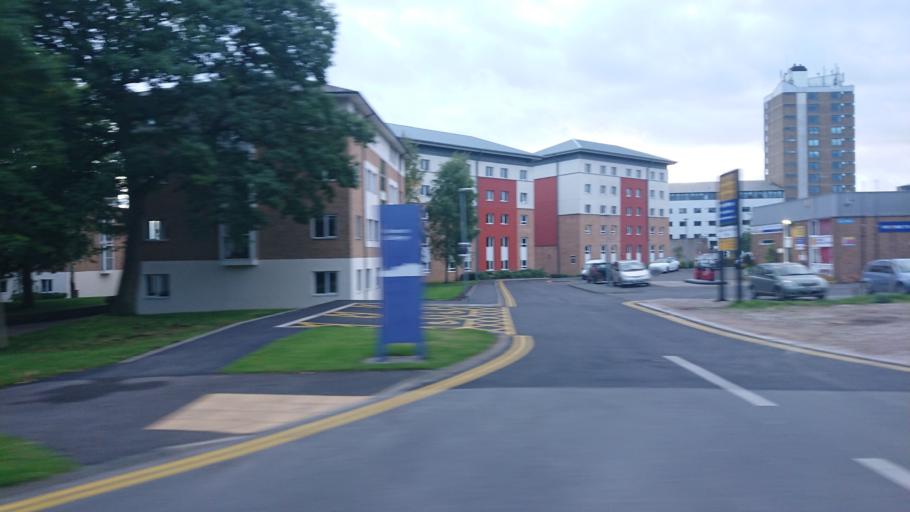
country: GB
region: England
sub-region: Lancashire
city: Galgate
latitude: 54.0095
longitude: -2.7824
